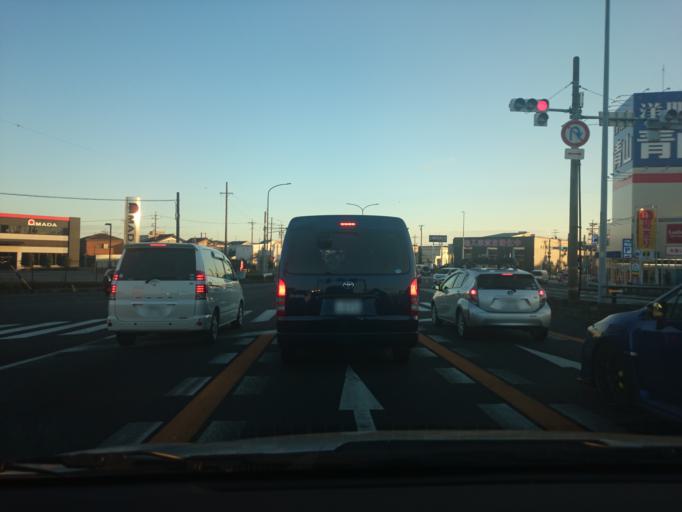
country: JP
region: Aichi
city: Ichinomiya
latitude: 35.3252
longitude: 136.8071
